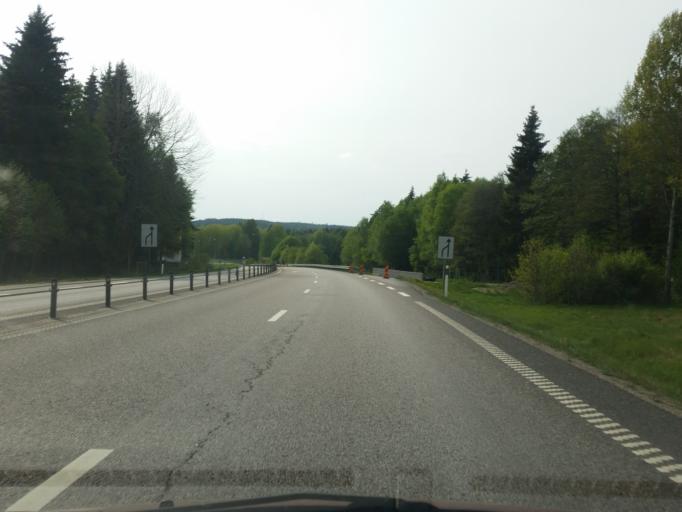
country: SE
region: Vaestra Goetaland
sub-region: Ulricehamns Kommun
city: Ulricehamn
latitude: 57.8023
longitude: 13.3790
